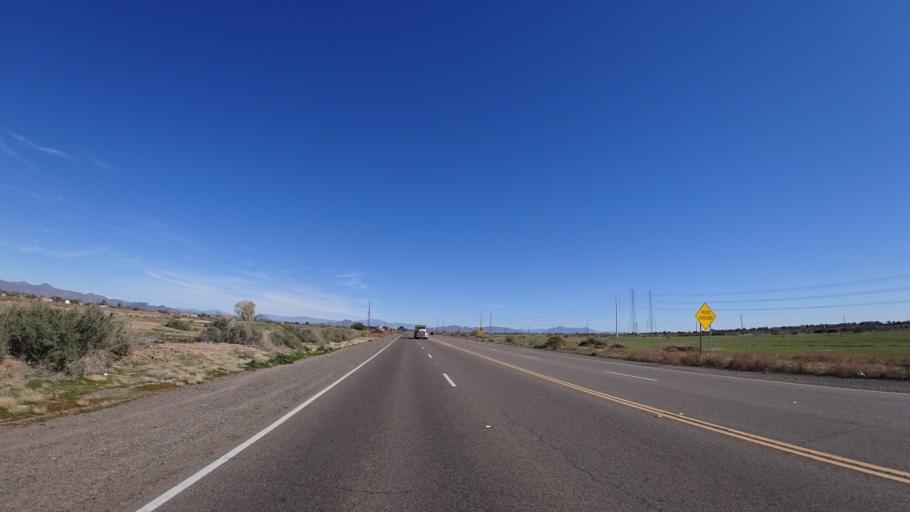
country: US
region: Arizona
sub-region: Maricopa County
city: Mesa
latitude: 33.4528
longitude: -111.8683
